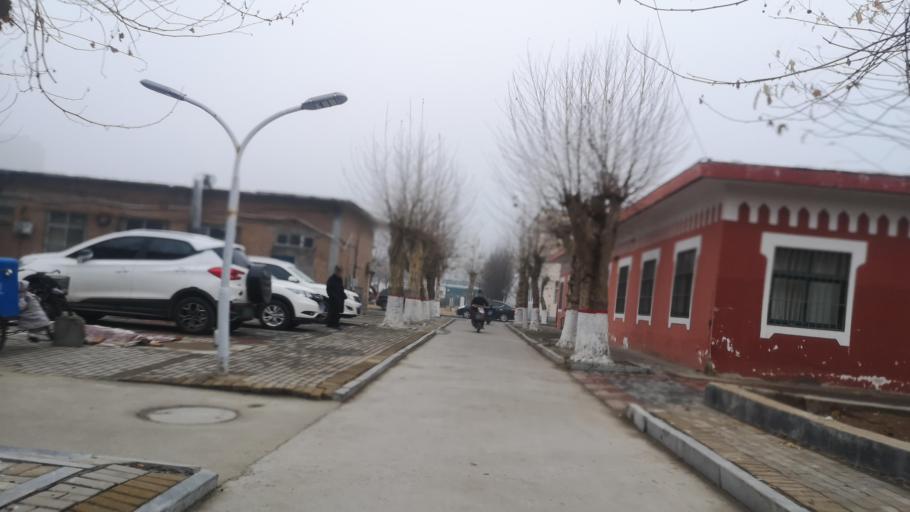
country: CN
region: Henan Sheng
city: Zhongyuanlu
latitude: 35.7637
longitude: 115.0712
